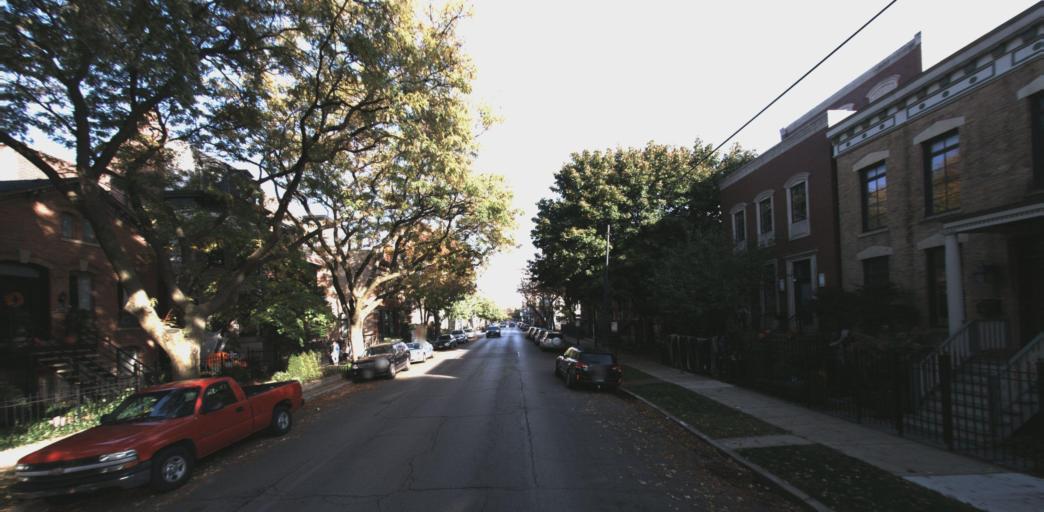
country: US
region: Illinois
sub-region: Cook County
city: Chicago
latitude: 41.9216
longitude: -87.6604
